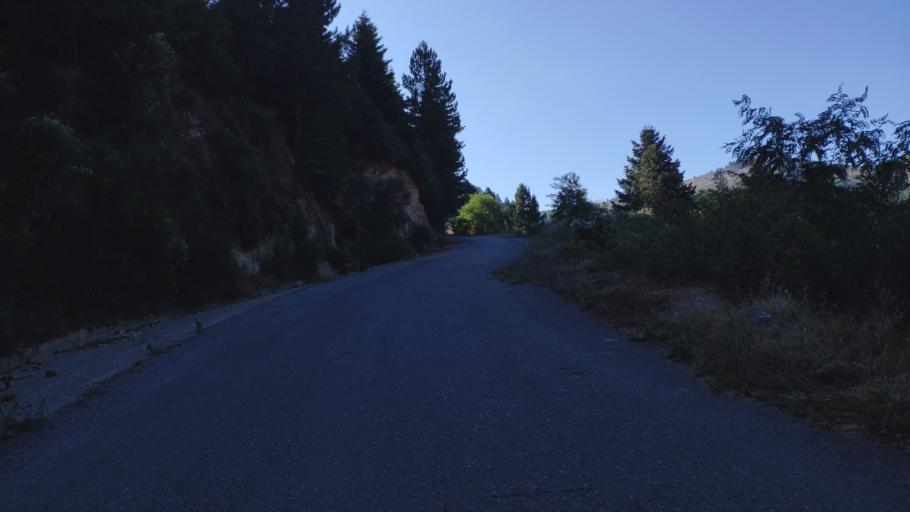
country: GR
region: Peloponnese
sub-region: Nomos Lakonias
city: Kariai
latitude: 37.1794
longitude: 22.5937
